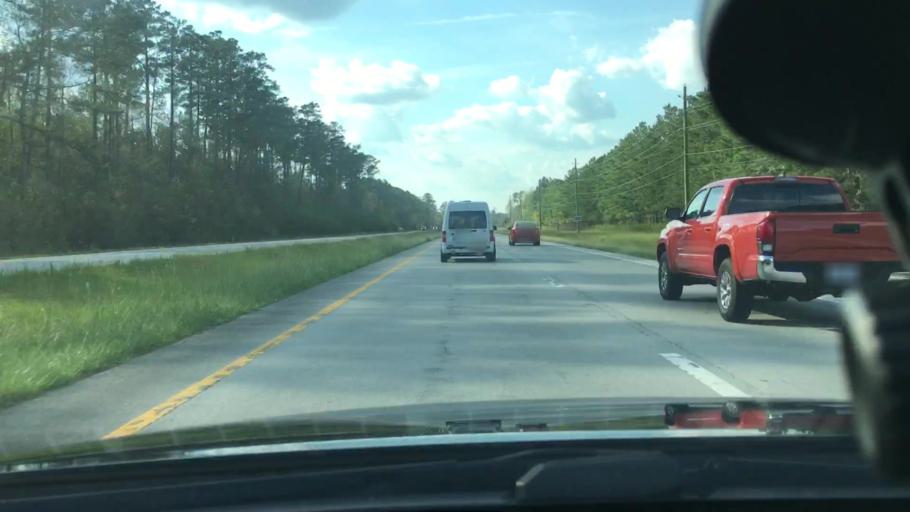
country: US
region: North Carolina
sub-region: Craven County
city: Neuse Forest
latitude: 34.9647
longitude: -76.9599
